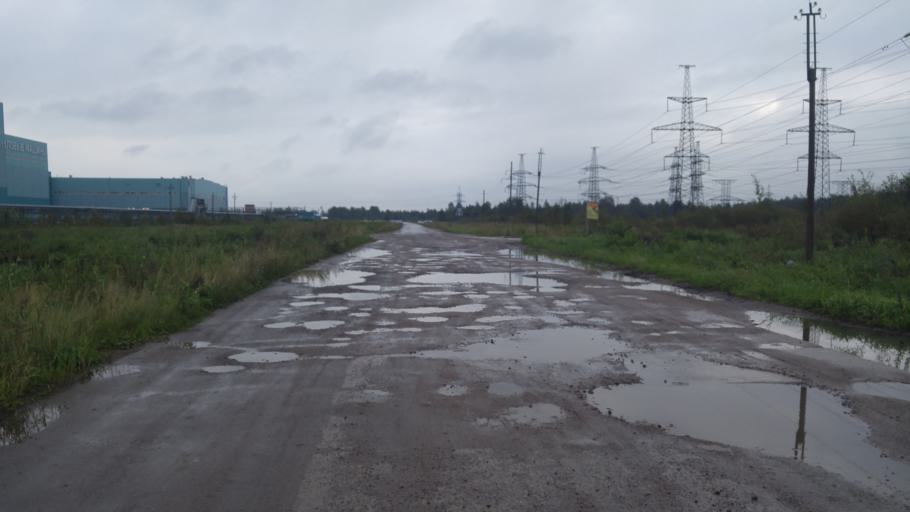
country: RU
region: St.-Petersburg
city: Metallostroy
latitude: 59.7783
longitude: 30.5623
